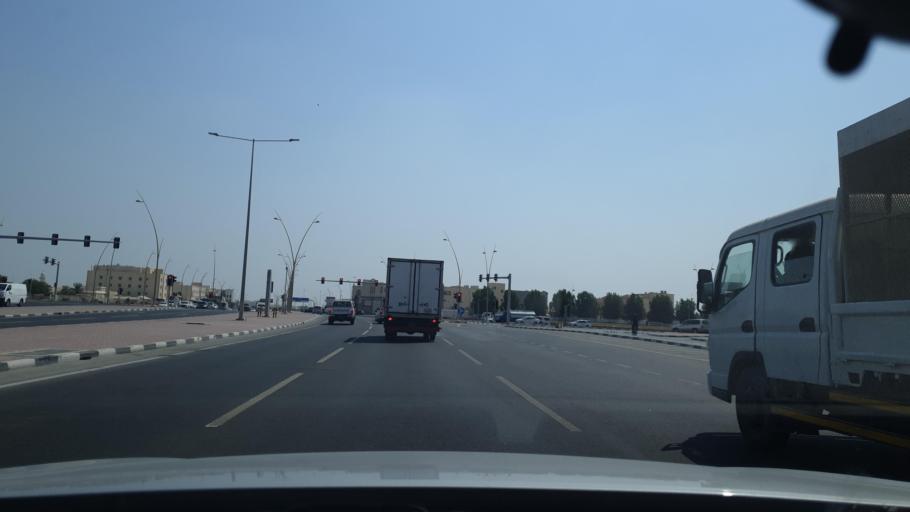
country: QA
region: Al Khawr
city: Al Khawr
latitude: 25.6814
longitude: 51.4961
